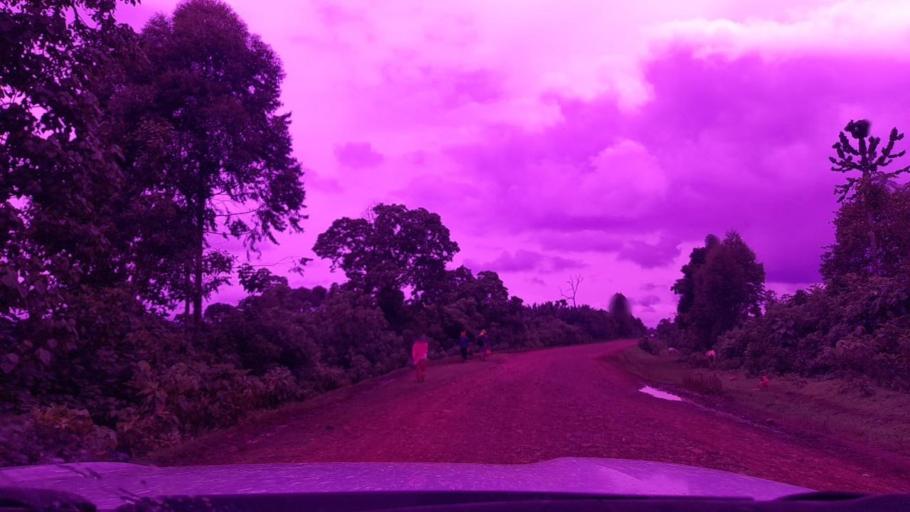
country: ET
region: Southern Nations, Nationalities, and People's Region
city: Tippi
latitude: 7.5732
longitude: 35.6396
